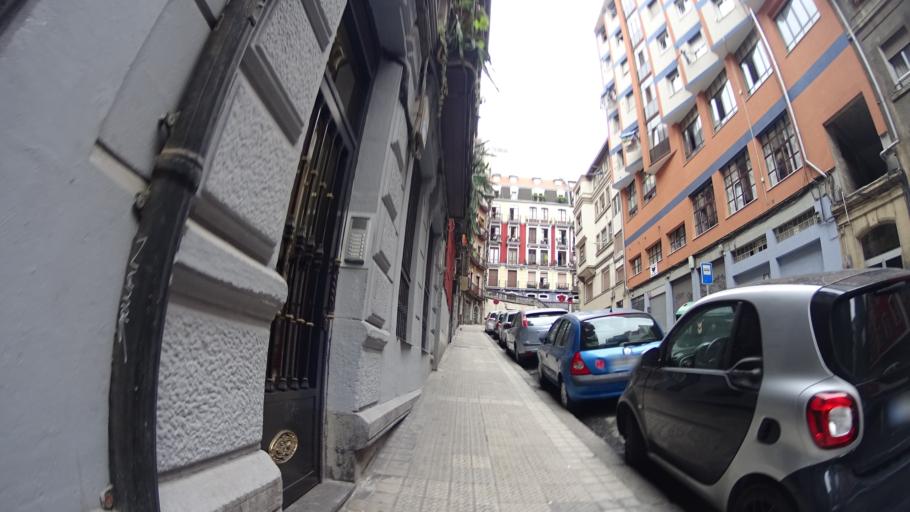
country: ES
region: Basque Country
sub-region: Bizkaia
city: Santutxu
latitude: 43.2571
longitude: -2.9187
